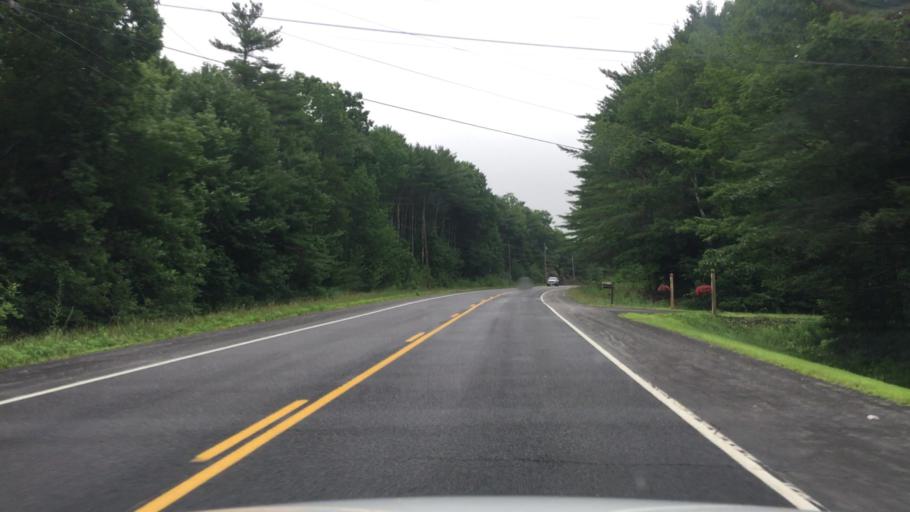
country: US
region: Maine
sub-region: Knox County
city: Union
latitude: 44.2143
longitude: -69.2354
